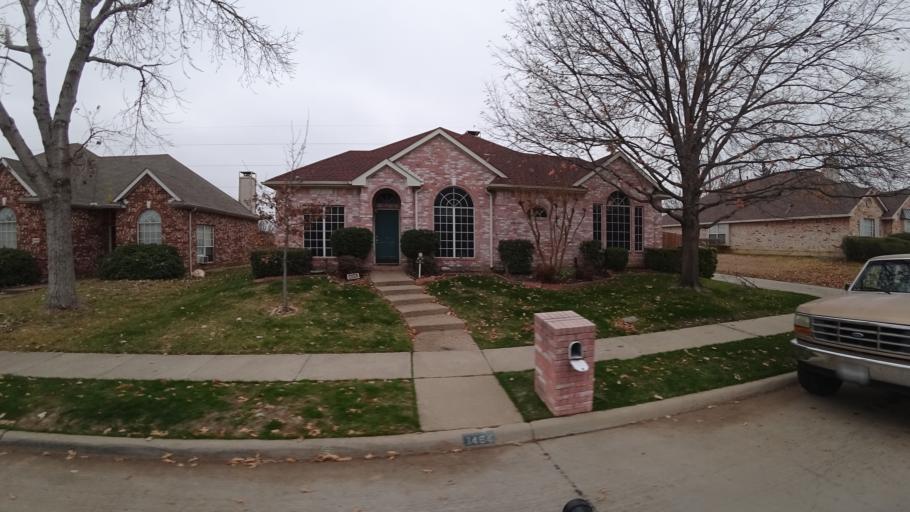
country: US
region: Texas
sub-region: Denton County
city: Highland Village
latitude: 33.0581
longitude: -97.0349
